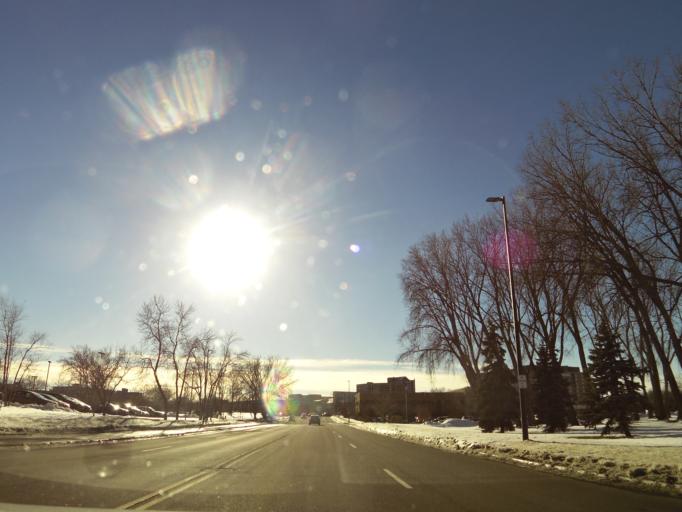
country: US
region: Minnesota
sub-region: Hennepin County
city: Saint Louis Park
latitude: 44.9396
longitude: -93.3406
